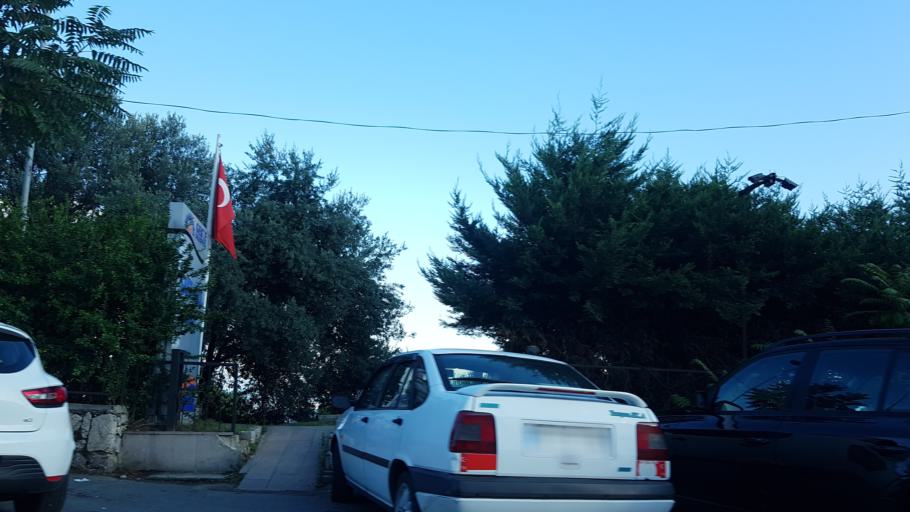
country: TR
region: Kocaeli
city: Darica
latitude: 40.7686
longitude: 29.4241
